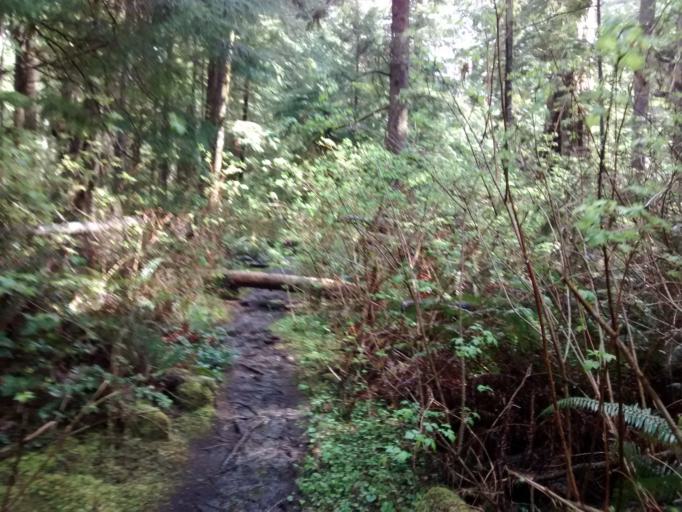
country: US
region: Washington
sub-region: Clallam County
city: Forks
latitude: 47.6750
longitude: -124.3903
